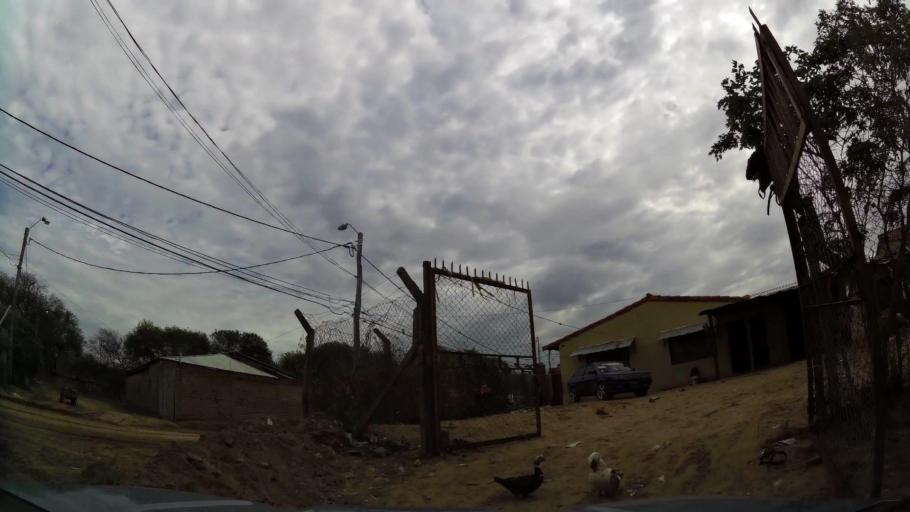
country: BO
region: Santa Cruz
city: Santa Cruz de la Sierra
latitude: -17.7373
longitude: -63.1936
